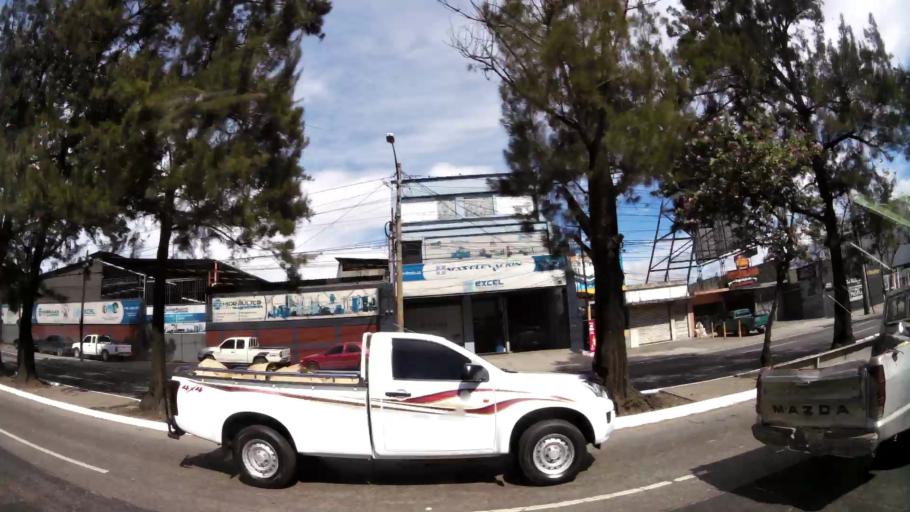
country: GT
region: Guatemala
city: Mixco
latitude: 14.6347
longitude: -90.5606
